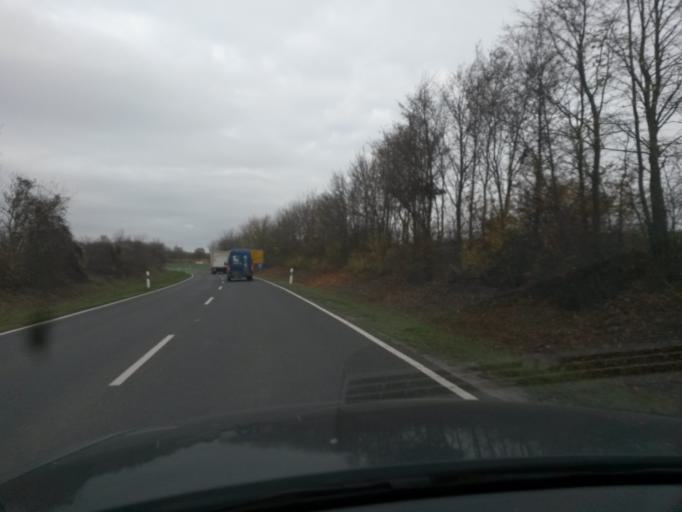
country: DE
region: Bavaria
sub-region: Regierungsbezirk Unterfranken
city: Estenfeld
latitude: 49.8351
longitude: 9.9890
